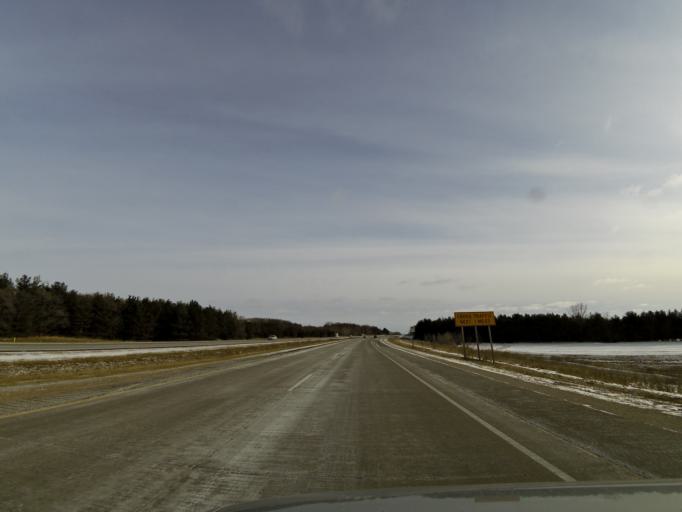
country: US
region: Minnesota
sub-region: Washington County
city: Lake Saint Croix Beach
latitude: 44.9306
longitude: -92.6840
